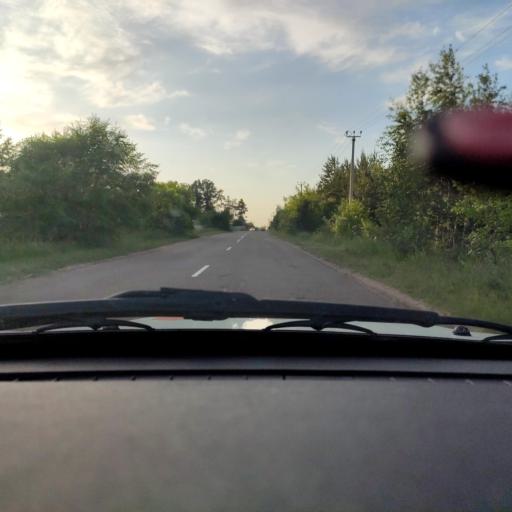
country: RU
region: Voronezj
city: Podgornoye
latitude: 51.8350
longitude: 39.2025
